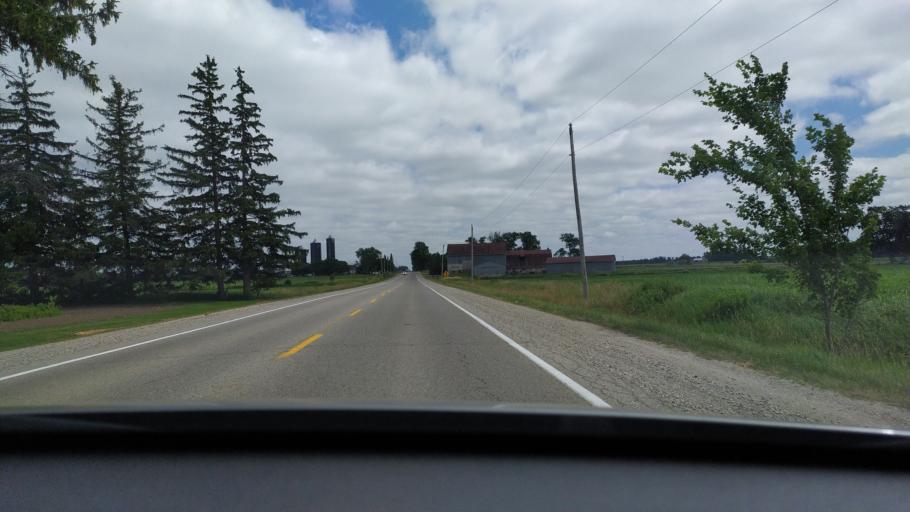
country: CA
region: Ontario
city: Stratford
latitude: 43.3375
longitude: -80.9637
